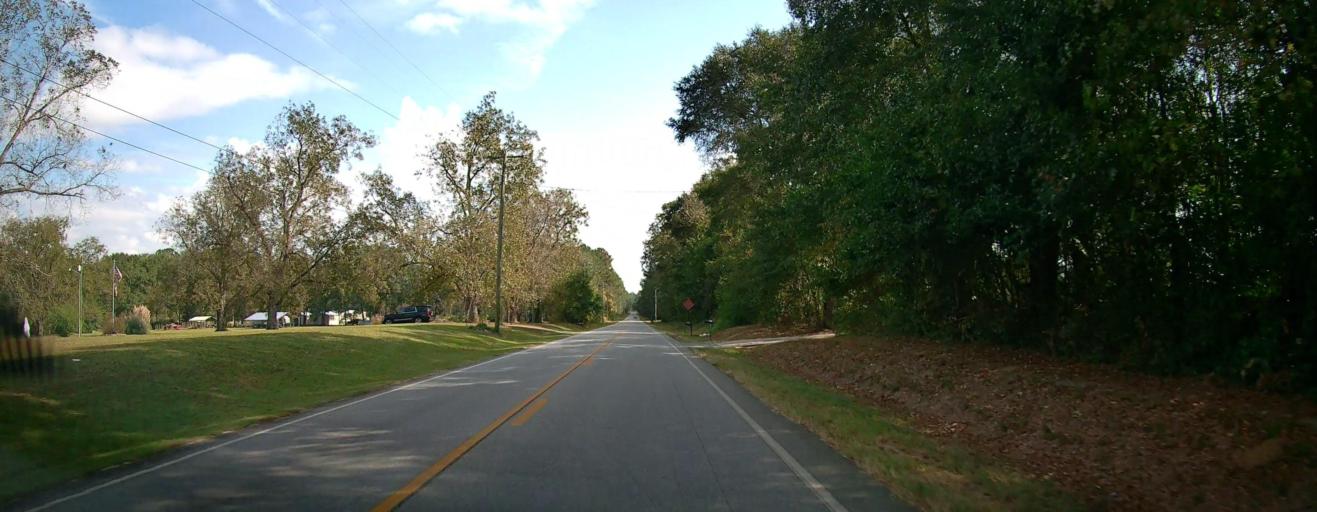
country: US
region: Georgia
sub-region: Thomas County
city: Thomasville
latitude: 30.9306
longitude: -84.0223
